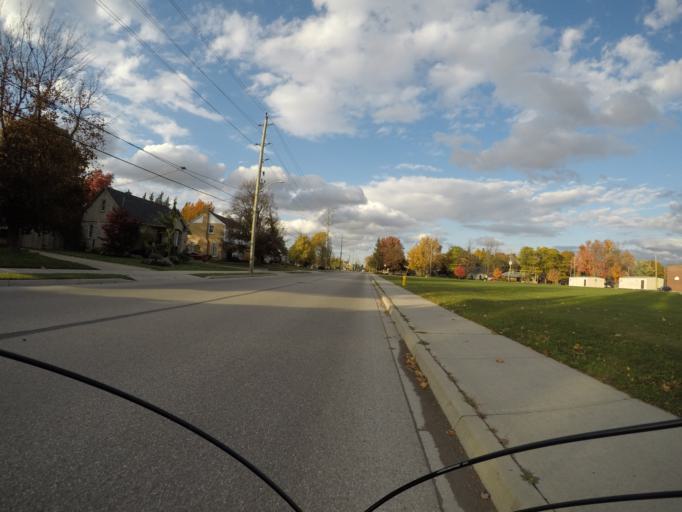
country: CA
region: Ontario
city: Waterloo
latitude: 43.5939
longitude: -80.5640
